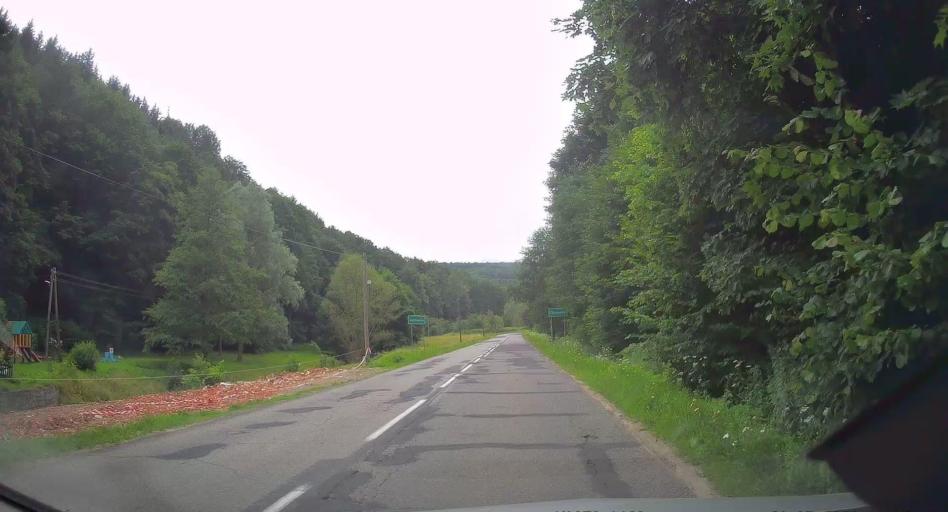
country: PL
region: Lower Silesian Voivodeship
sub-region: Powiat walbrzyski
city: Jedlina-Zdroj
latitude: 50.7294
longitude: 16.3893
